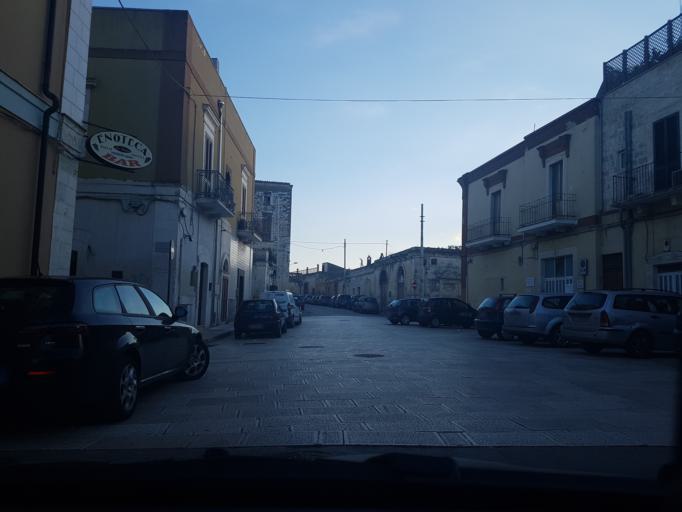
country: IT
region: Apulia
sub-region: Provincia di Bari
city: Bitritto
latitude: 41.0418
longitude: 16.8250
